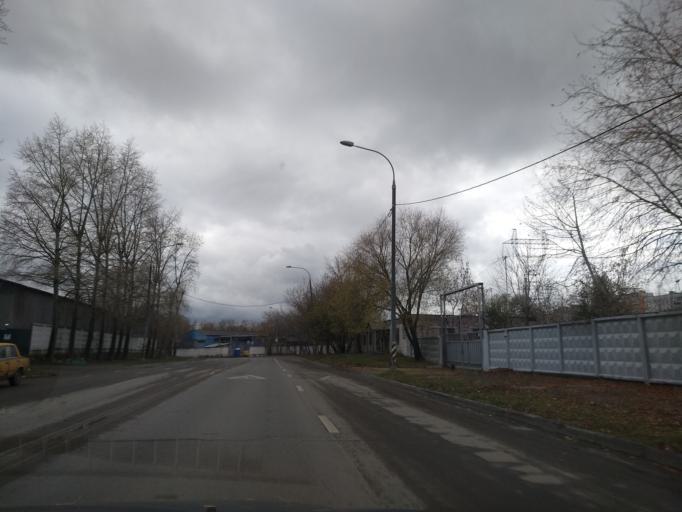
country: RU
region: Moscow
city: Kozeyevo
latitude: 55.8867
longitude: 37.6230
